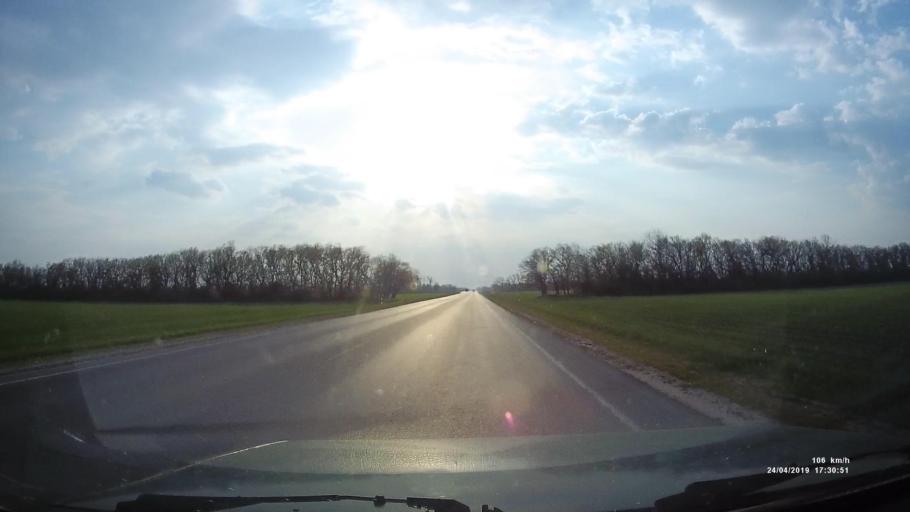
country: RU
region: Rostov
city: Tselina
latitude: 46.5229
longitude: 41.1323
